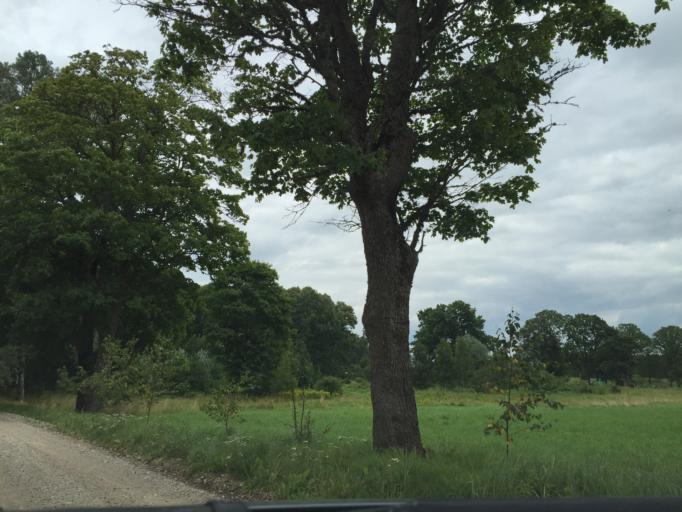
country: LV
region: Seja
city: Loja
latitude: 57.1455
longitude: 24.6626
